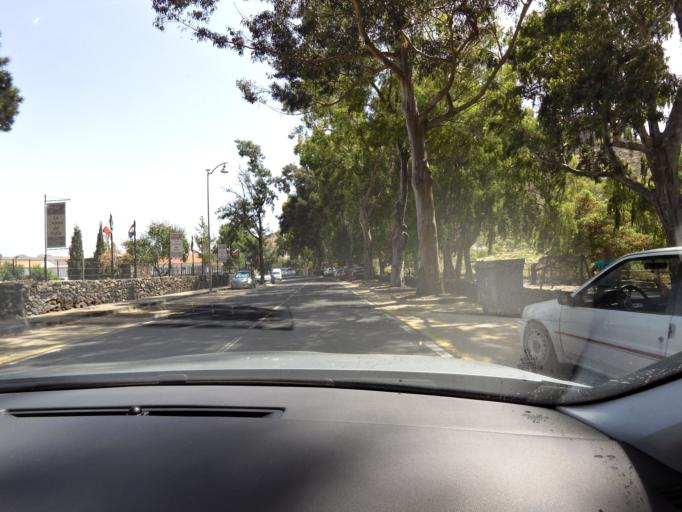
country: ES
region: Canary Islands
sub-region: Provincia de Santa Cruz de Tenerife
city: Santiago del Teide
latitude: 28.2986
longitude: -16.8161
